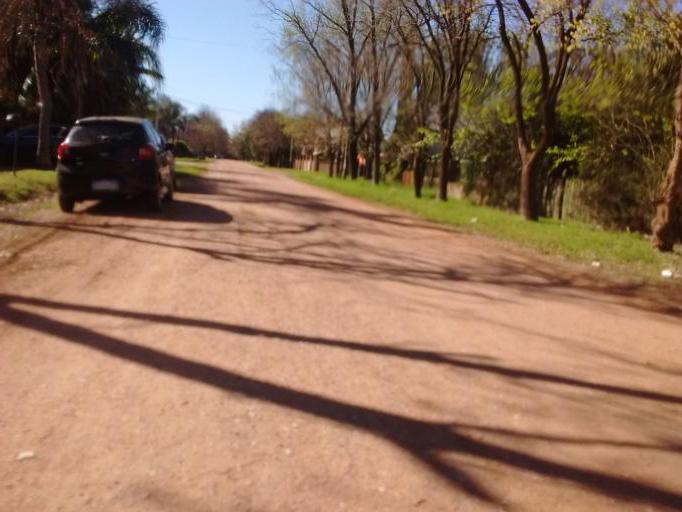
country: AR
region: Santa Fe
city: Funes
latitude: -32.9274
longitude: -60.8139
